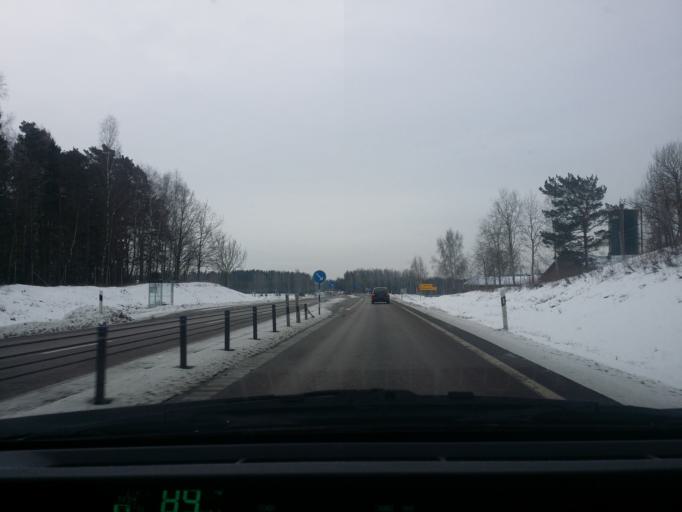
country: SE
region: Vaestra Goetaland
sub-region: Skovde Kommun
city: Stopen
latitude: 58.5343
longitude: 13.8145
